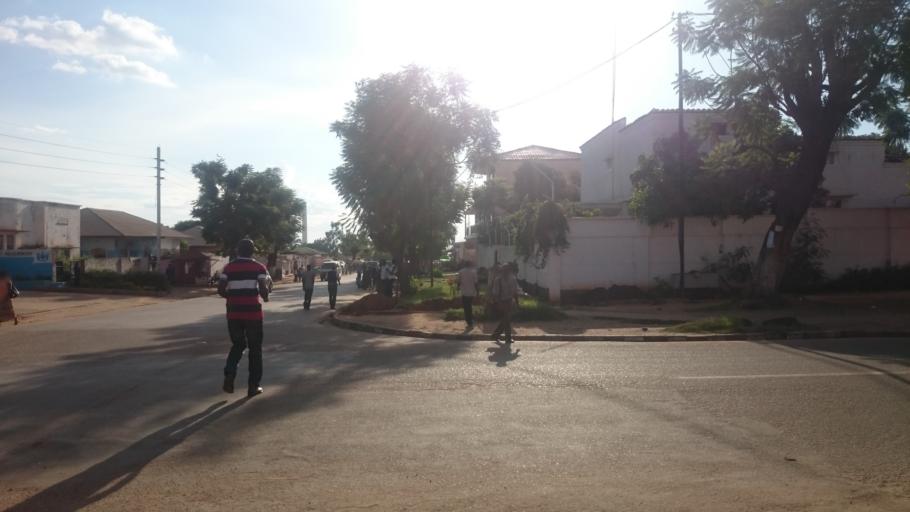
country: CD
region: Katanga
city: Lubumbashi
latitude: -11.6724
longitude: 27.4826
